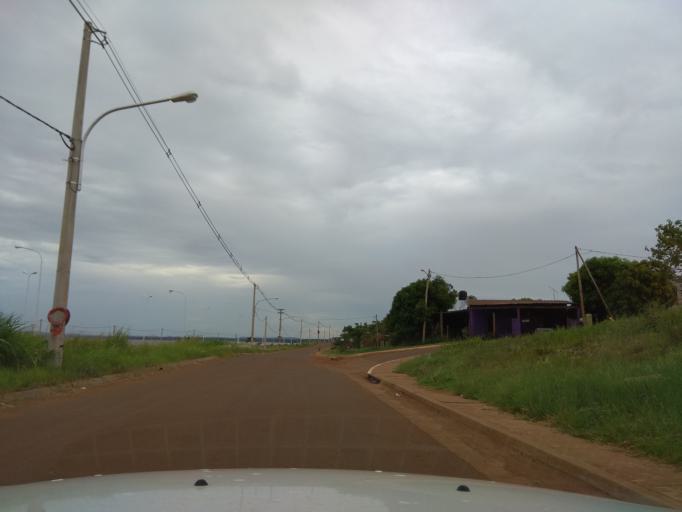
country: AR
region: Misiones
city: Garupa
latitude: -27.4365
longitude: -55.8594
